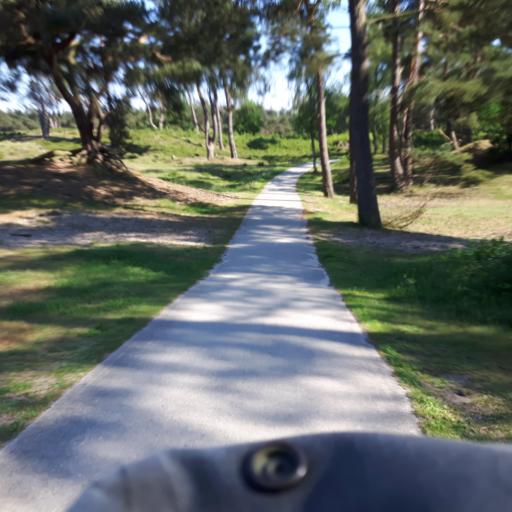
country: NL
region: Utrecht
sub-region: Gemeente Soest
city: Soest
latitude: 52.1531
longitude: 5.3219
